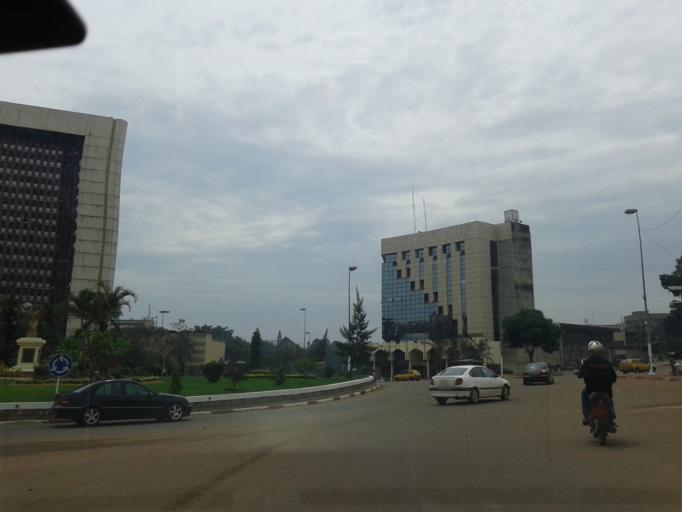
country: CM
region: Centre
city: Yaounde
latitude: 3.8656
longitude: 11.5157
